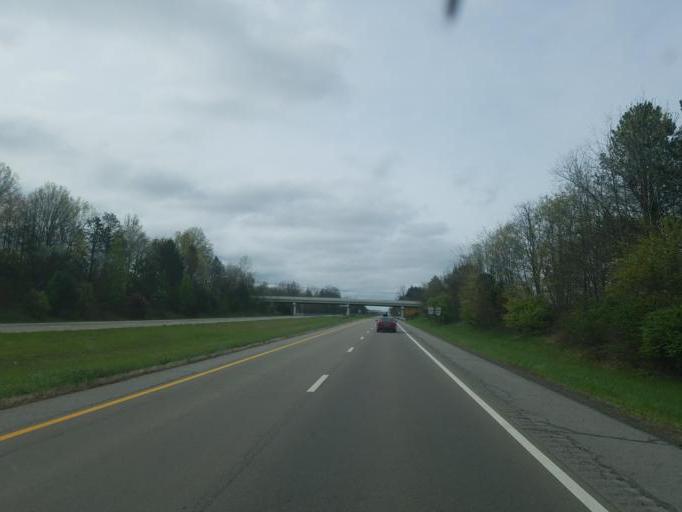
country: US
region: Ohio
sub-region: Wayne County
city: Wooster
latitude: 40.7865
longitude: -81.9147
